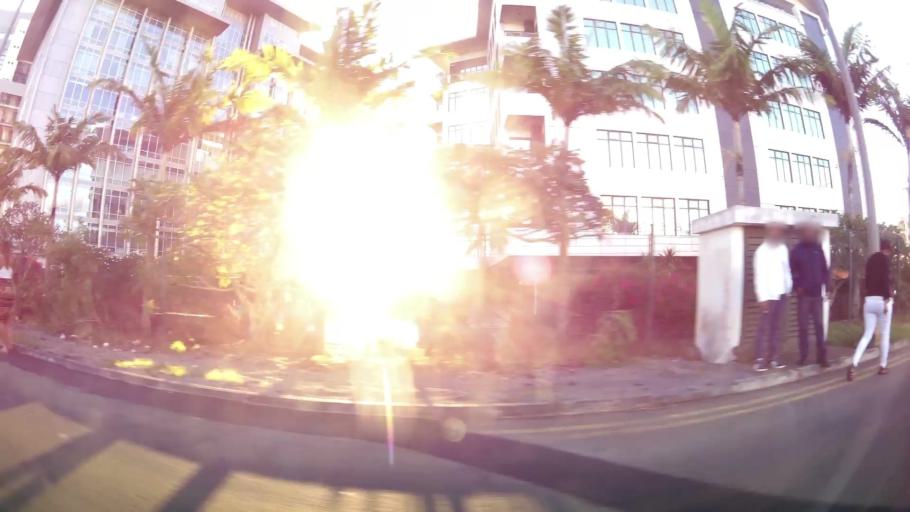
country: MU
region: Plaines Wilhems
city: Ebene
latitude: -20.2444
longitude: 57.4940
